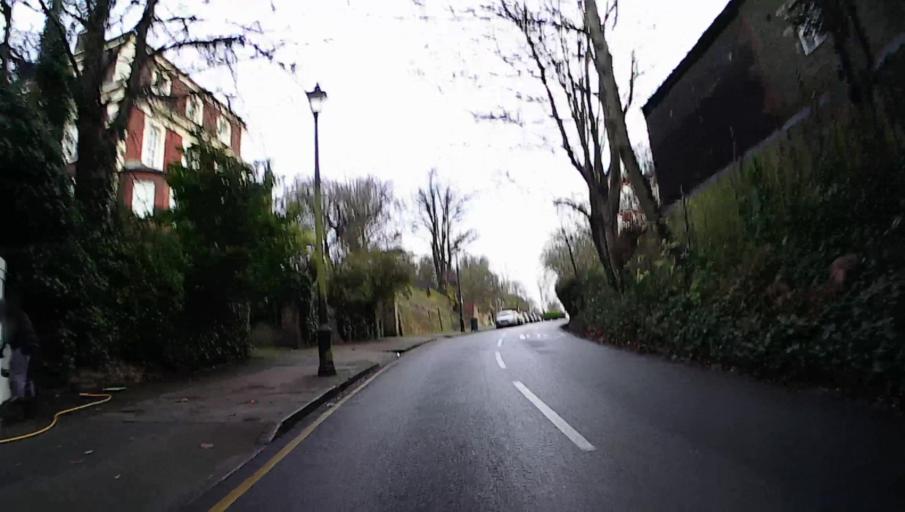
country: GB
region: England
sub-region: Greater London
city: Blackheath
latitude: 51.4758
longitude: -0.0048
